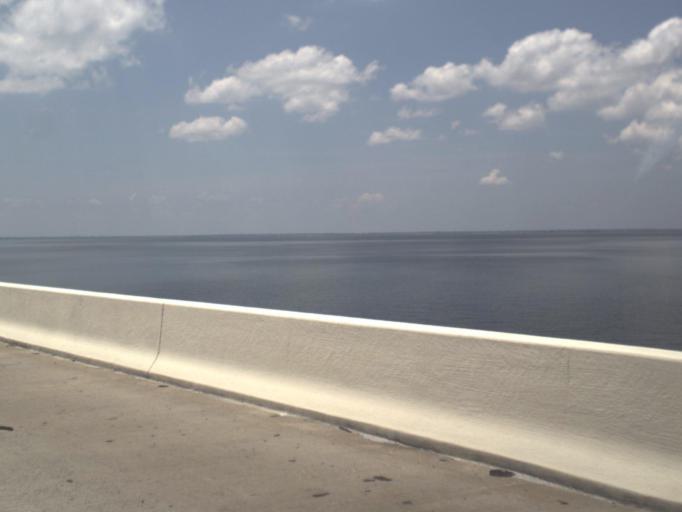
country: US
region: Florida
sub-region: Pinellas County
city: Gandy
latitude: 27.9317
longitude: -82.5776
